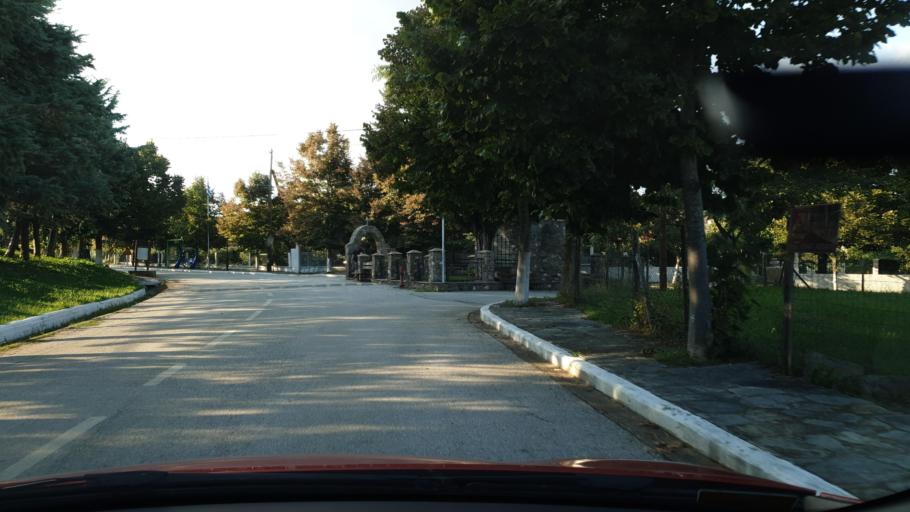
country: GR
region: Central Macedonia
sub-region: Nomos Chalkidikis
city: Galatista
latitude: 40.5181
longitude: 23.2840
